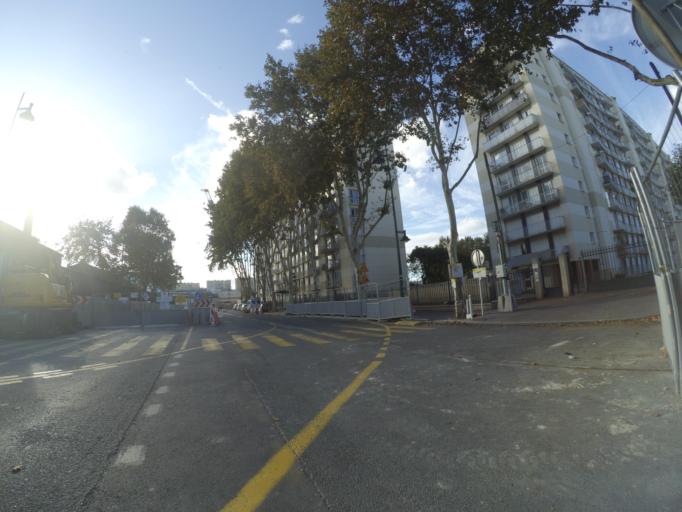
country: FR
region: Ile-de-France
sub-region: Departement des Hauts-de-Seine
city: Montrouge
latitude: 48.8108
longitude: 2.3051
